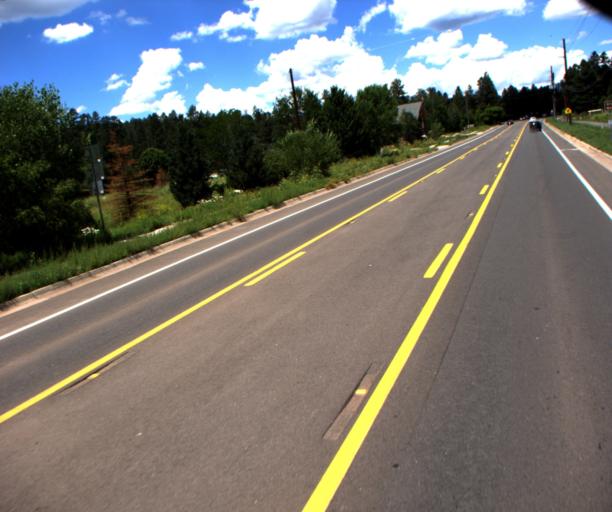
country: US
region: Arizona
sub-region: Coconino County
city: Flagstaff
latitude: 35.2254
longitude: -111.6577
